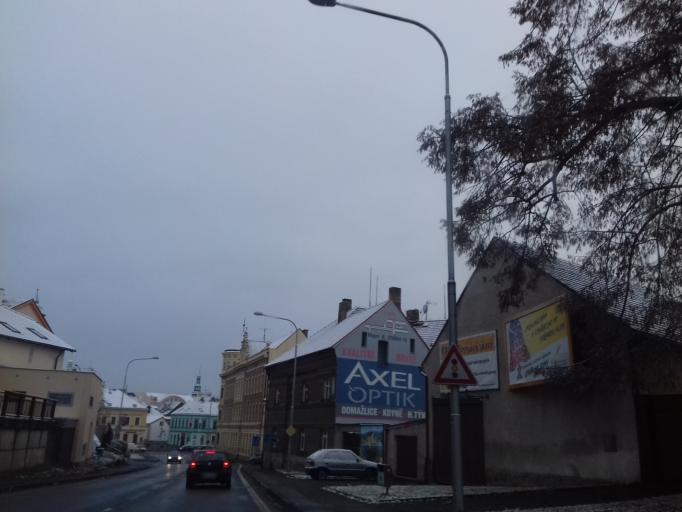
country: CZ
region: Plzensky
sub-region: Okres Domazlice
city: Domazlice
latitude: 49.4431
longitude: 12.9301
